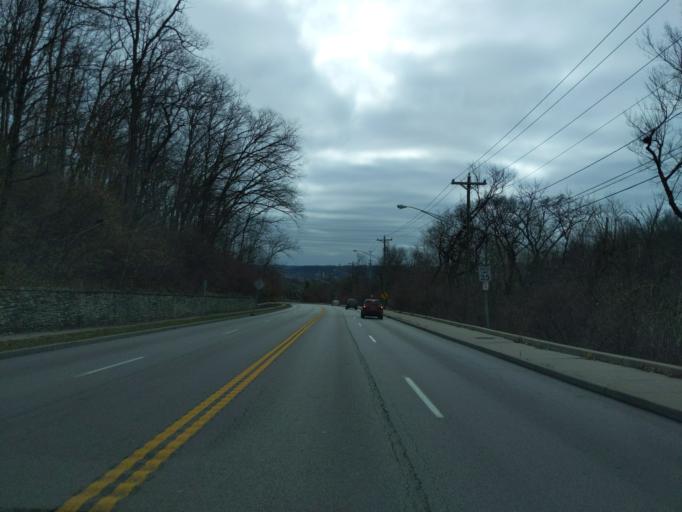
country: US
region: Ohio
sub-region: Hamilton County
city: Finneytown
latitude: 39.1836
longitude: -84.5443
